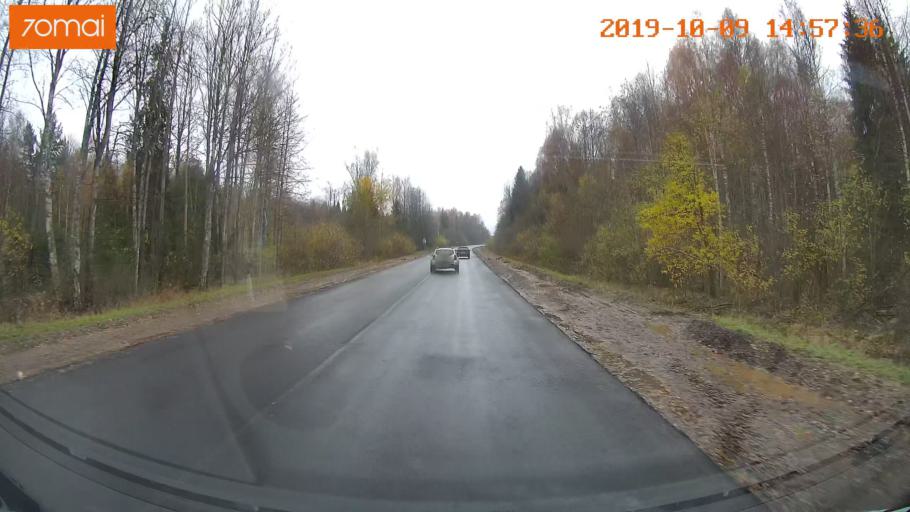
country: RU
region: Kostroma
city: Chistyye Bory
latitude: 58.3360
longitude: 41.6515
